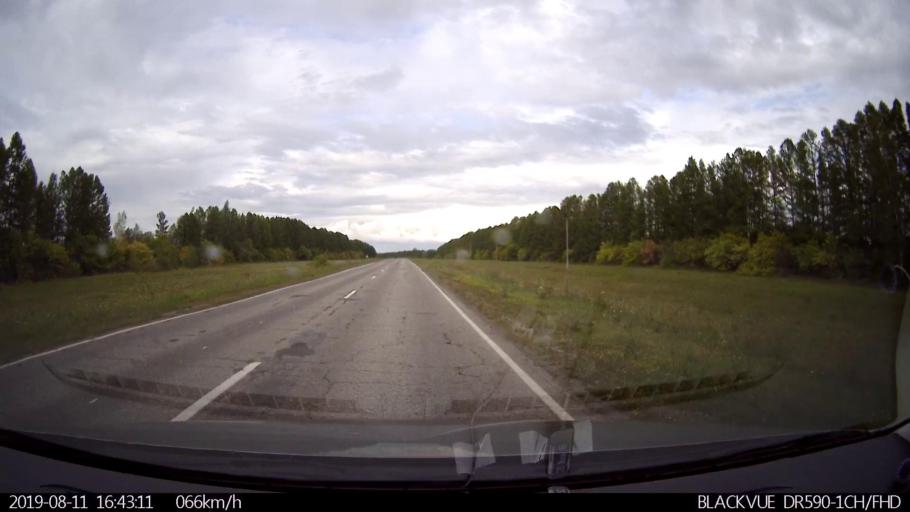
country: RU
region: Ulyanovsk
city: Mayna
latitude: 54.1666
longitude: 47.6694
